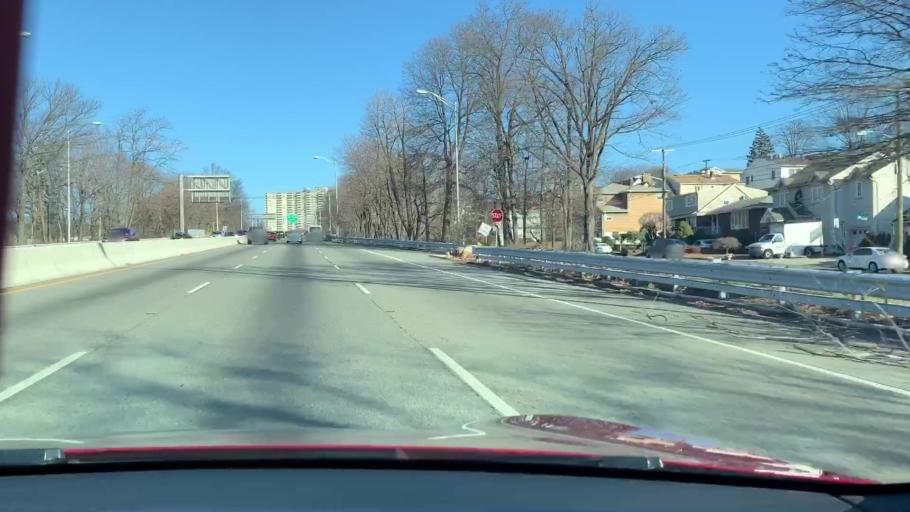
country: US
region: New Jersey
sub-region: Bergen County
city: Palisades Park
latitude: 40.8478
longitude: -73.9891
